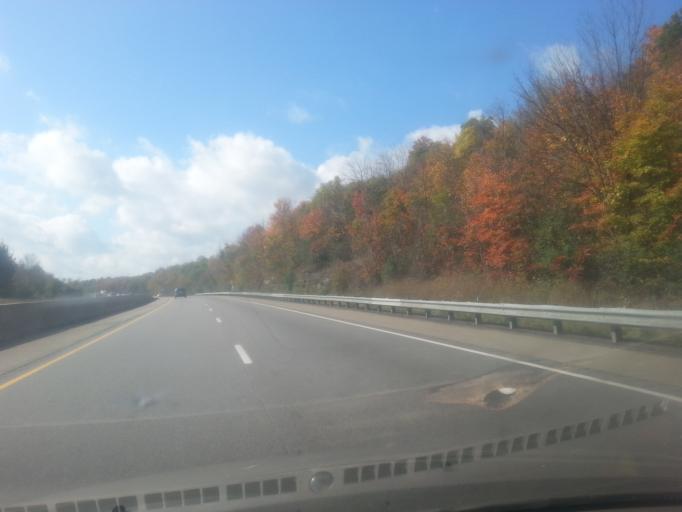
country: CA
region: Ontario
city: Brockville
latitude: 44.5526
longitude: -75.7626
